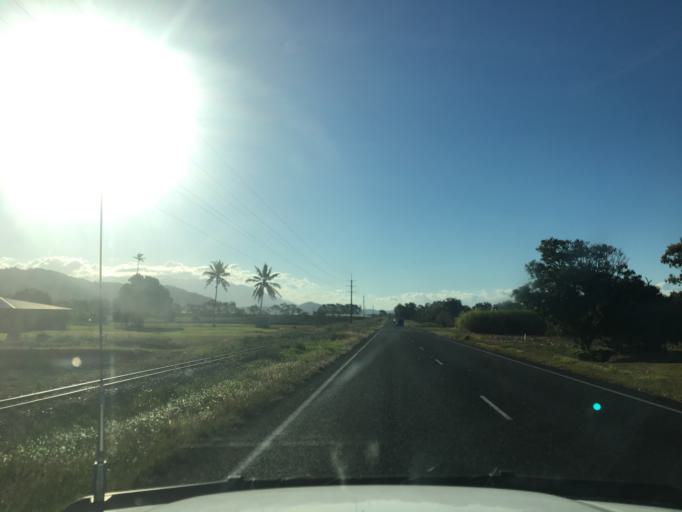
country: AU
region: Queensland
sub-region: Cairns
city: Port Douglas
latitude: -16.5140
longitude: 145.4456
